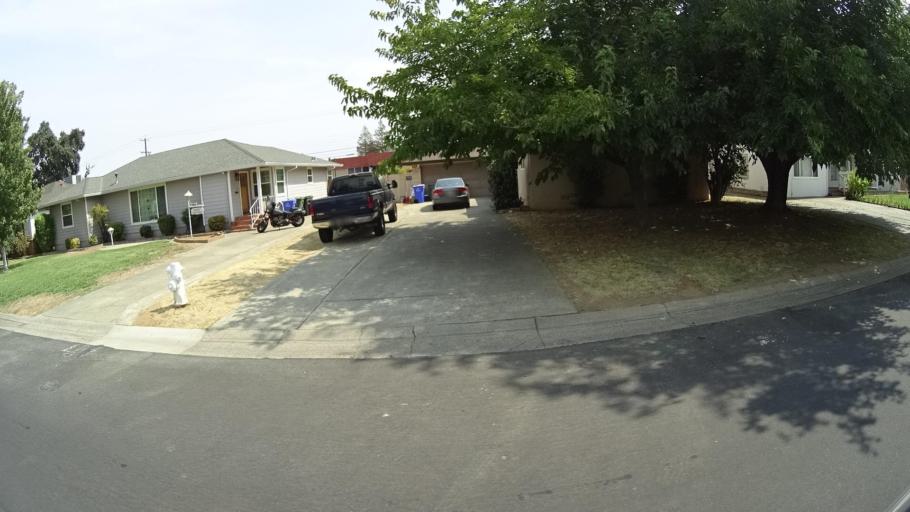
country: US
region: California
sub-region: Sacramento County
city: Elk Grove
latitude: 38.4107
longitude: -121.3749
